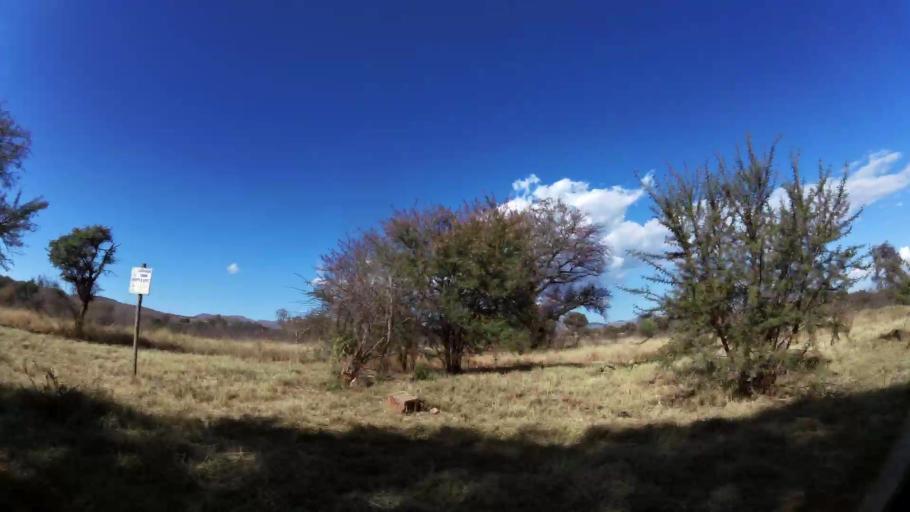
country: ZA
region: Limpopo
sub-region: Waterberg District Municipality
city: Mokopane
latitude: -24.2020
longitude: 29.0130
